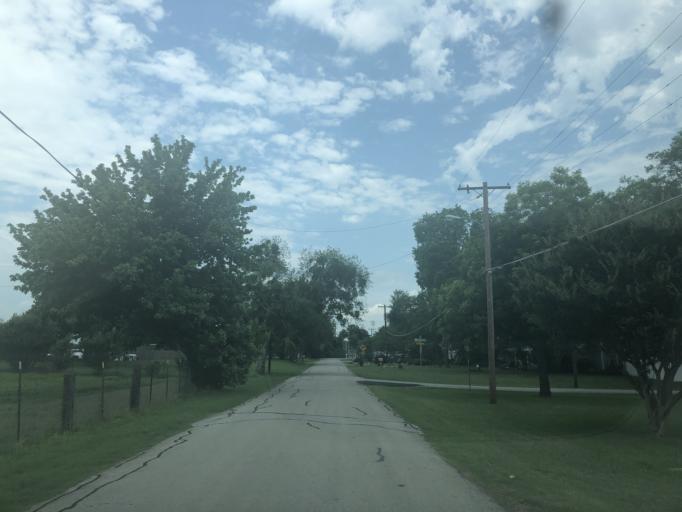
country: US
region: Texas
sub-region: Dallas County
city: Irving
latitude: 32.7911
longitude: -96.9417
